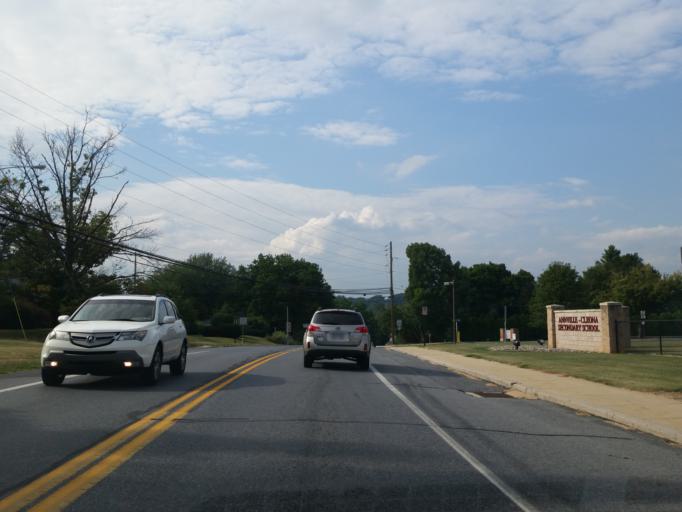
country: US
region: Pennsylvania
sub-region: Lebanon County
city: Annville
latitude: 40.3229
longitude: -76.5114
